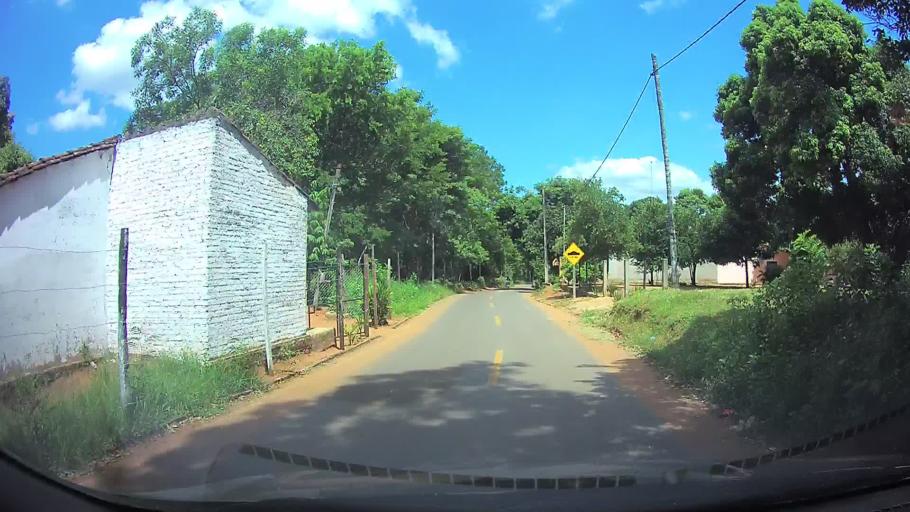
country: PY
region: Central
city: Aregua
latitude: -25.2872
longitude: -57.4132
